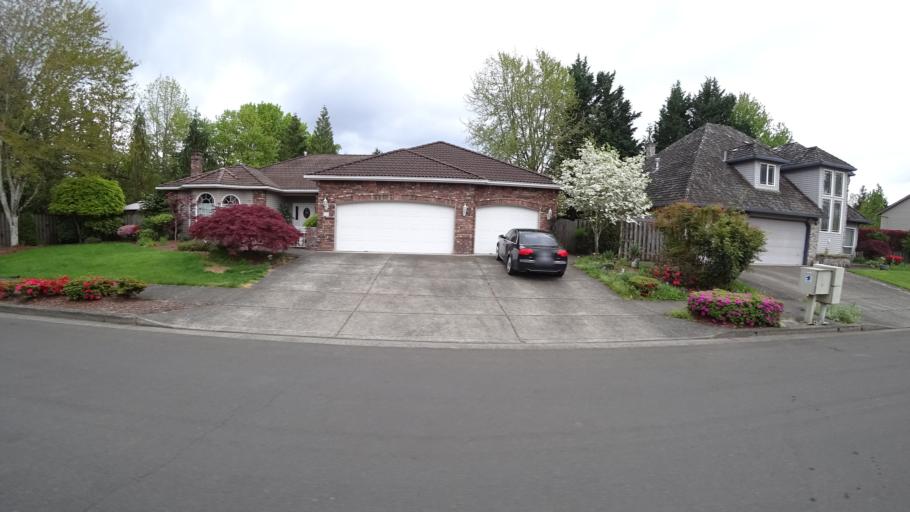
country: US
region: Oregon
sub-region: Washington County
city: Hillsboro
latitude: 45.5490
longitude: -122.9802
